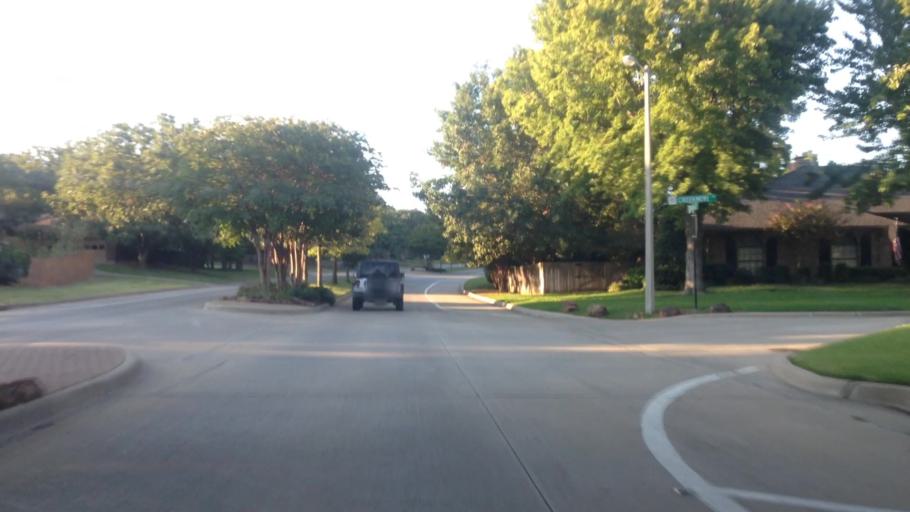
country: US
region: Texas
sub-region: Denton County
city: Trophy Club
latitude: 32.9964
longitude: -97.1687
